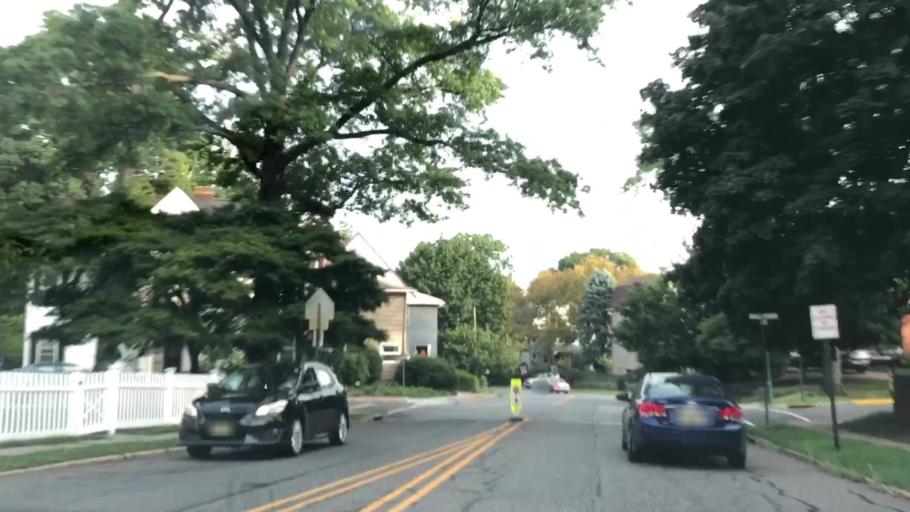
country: US
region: New Jersey
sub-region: Essex County
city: Glen Ridge
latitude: 40.8020
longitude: -74.2016
